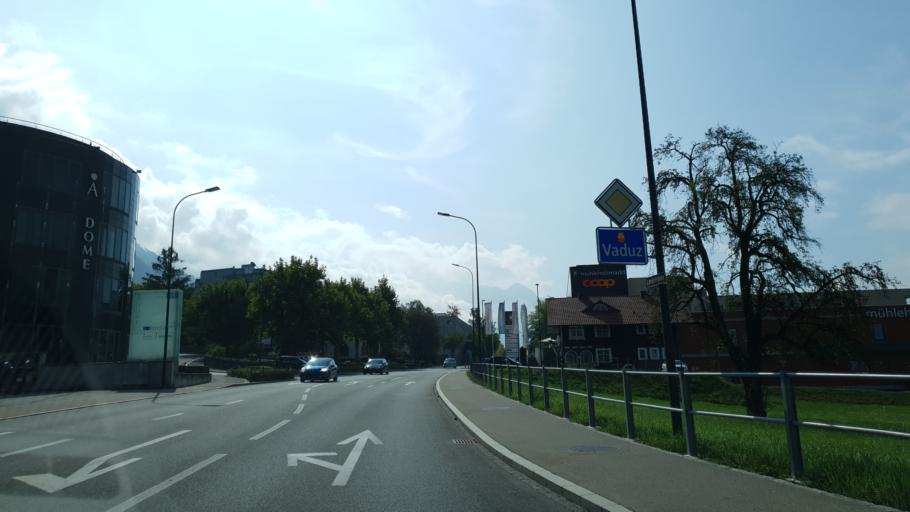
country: LI
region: Schaan
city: Schaan
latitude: 47.1559
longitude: 9.5100
